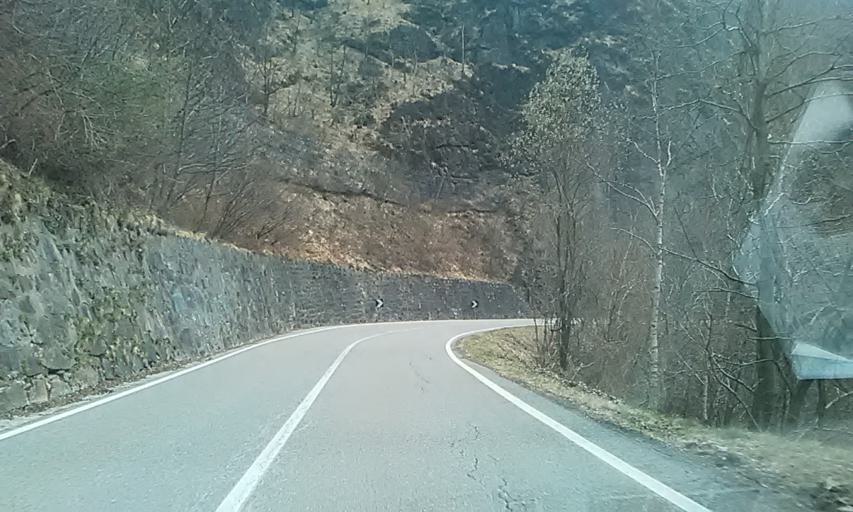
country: IT
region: Piedmont
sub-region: Provincia di Vercelli
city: Cervatto
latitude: 45.8807
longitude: 8.1755
